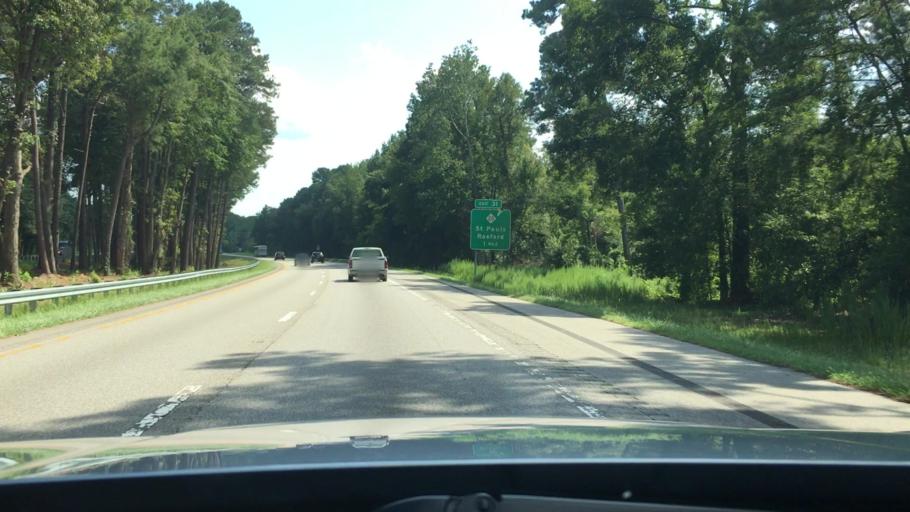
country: US
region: North Carolina
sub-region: Robeson County
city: Saint Pauls
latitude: 34.8291
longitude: -78.9821
